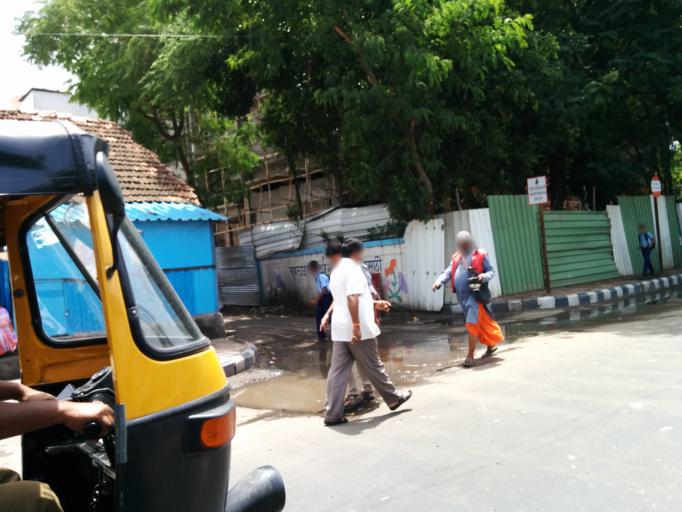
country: IN
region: Maharashtra
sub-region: Pune Division
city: Lohogaon
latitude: 18.5334
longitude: 73.9305
